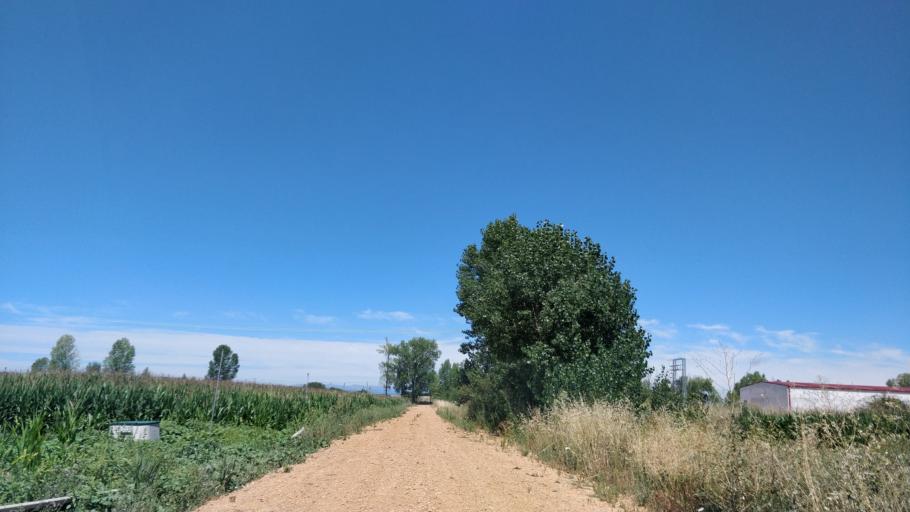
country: ES
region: Castille and Leon
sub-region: Provincia de Leon
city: Bustillo del Paramo
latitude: 42.4772
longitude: -5.8108
